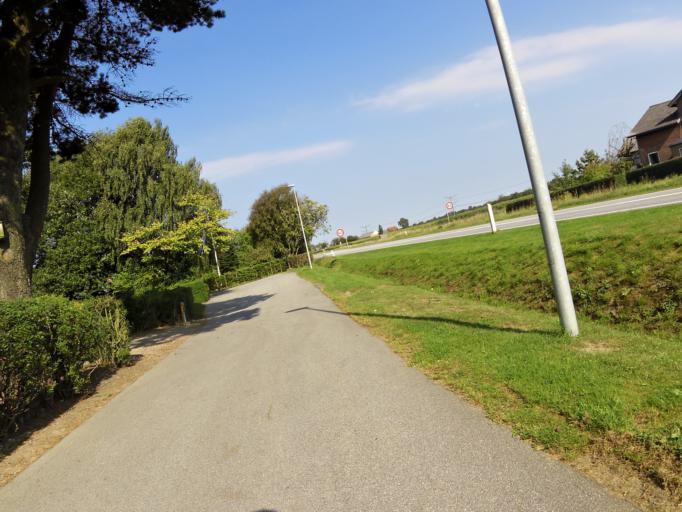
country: DK
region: South Denmark
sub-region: Vejen Kommune
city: Vejen
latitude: 55.4115
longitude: 9.1550
